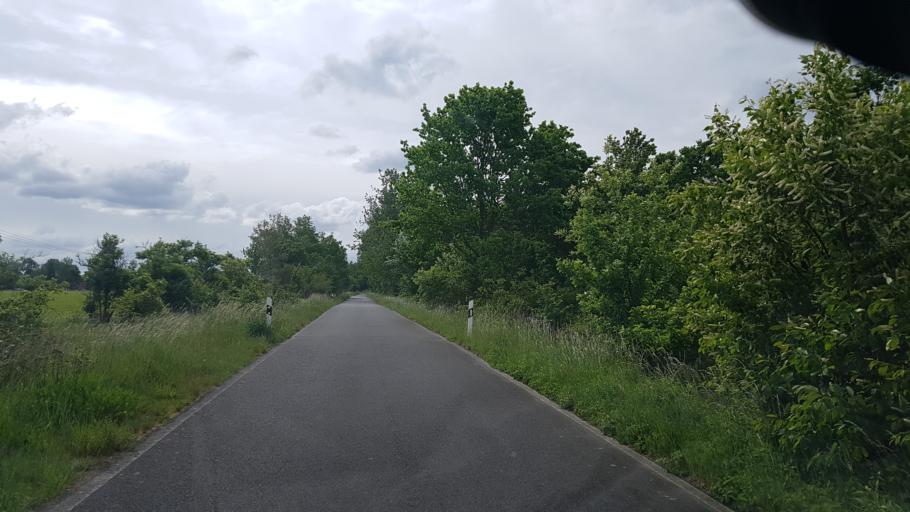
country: DE
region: Brandenburg
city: Crinitz
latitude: 51.8108
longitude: 13.8100
